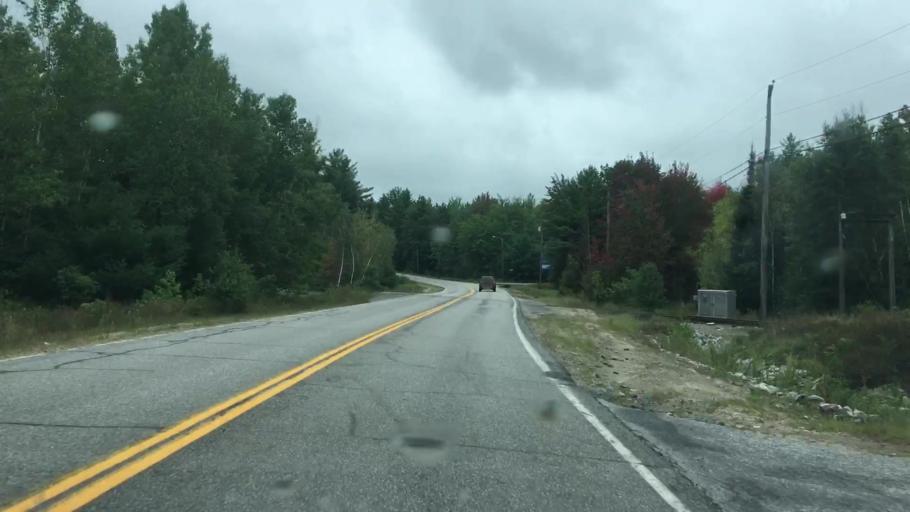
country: US
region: Maine
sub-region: Oxford County
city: Brownfield
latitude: 43.9858
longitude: -70.9322
